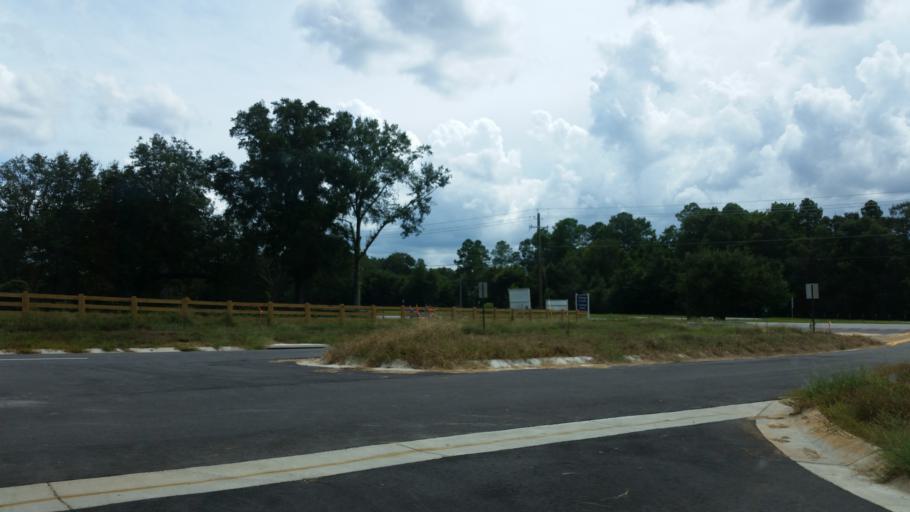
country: US
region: Florida
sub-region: Escambia County
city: Cantonment
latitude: 30.5359
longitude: -87.4108
